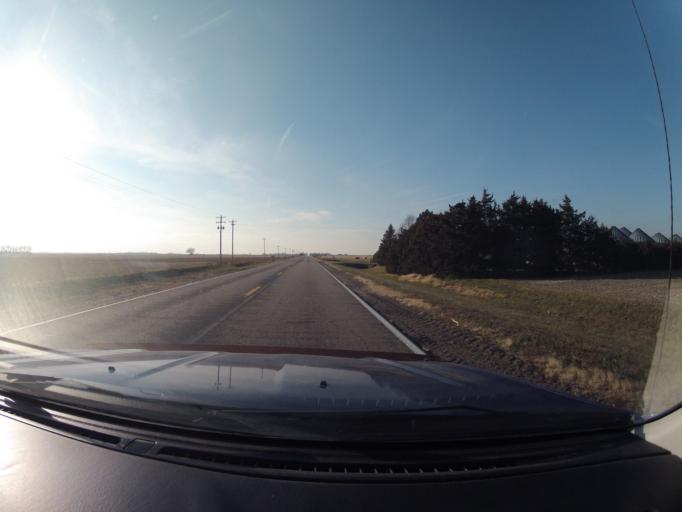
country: US
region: Nebraska
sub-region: Buffalo County
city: Kearney
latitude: 40.6410
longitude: -99.0554
